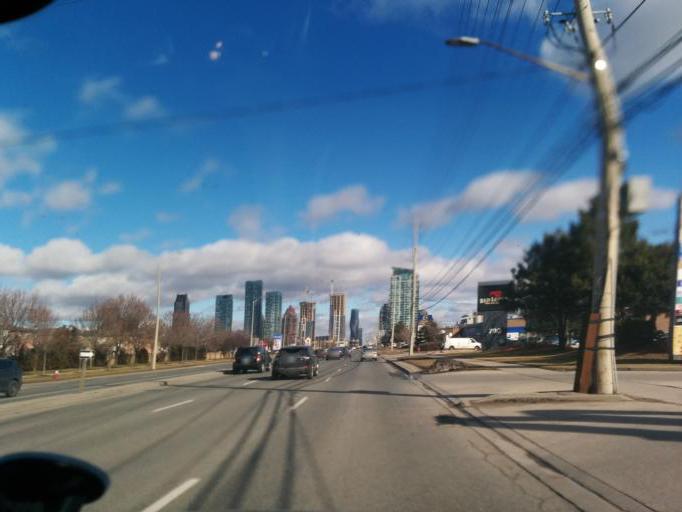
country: CA
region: Ontario
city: Mississauga
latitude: 43.5763
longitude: -79.6546
